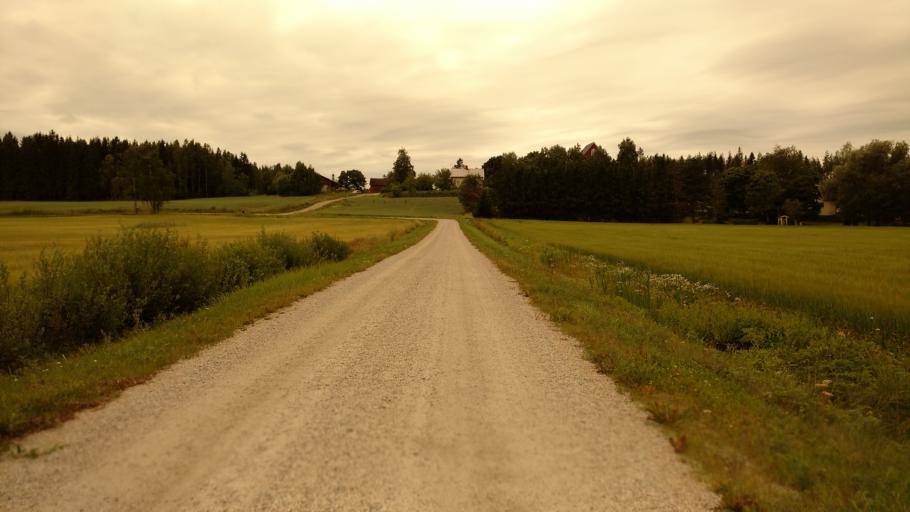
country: FI
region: Varsinais-Suomi
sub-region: Turku
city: Paimio
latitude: 60.4186
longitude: 22.8341
